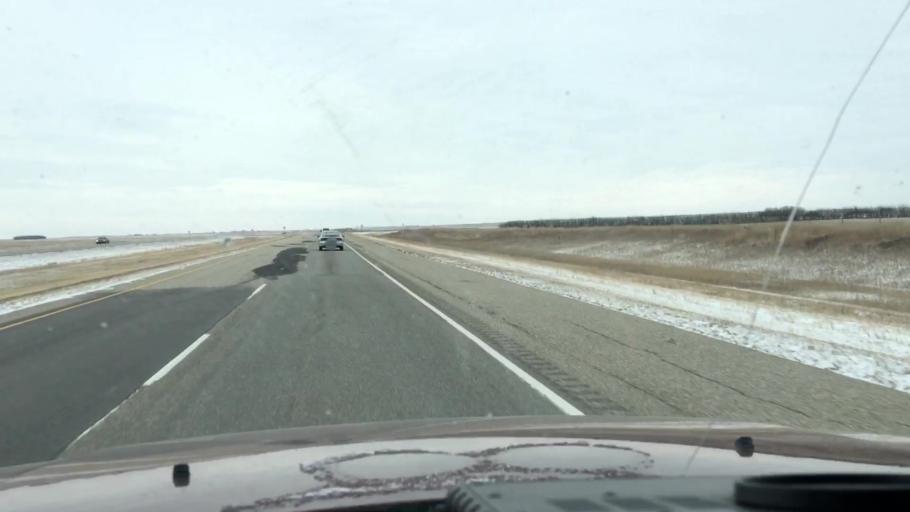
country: CA
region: Saskatchewan
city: Saskatoon
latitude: 51.4662
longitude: -106.2415
